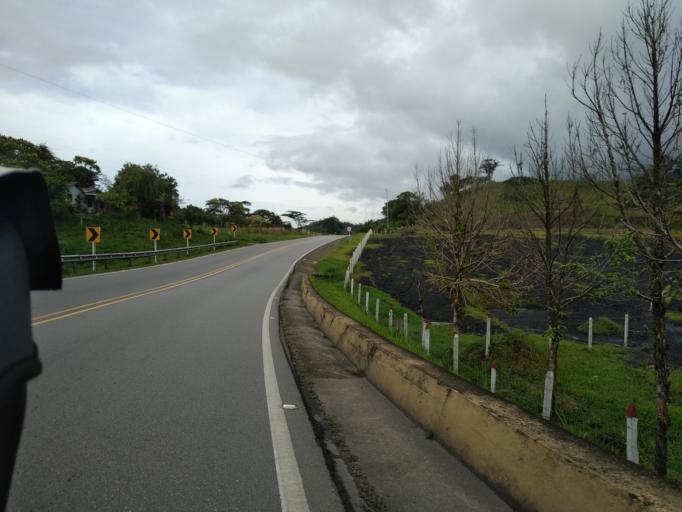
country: CO
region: Santander
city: Suaita
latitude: 6.1260
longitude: -73.3623
